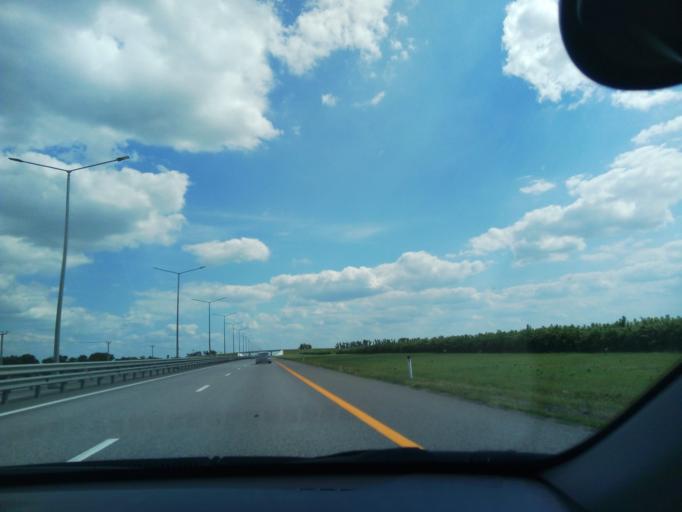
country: RU
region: Voronezj
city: Podkletnoye
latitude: 51.5760
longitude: 39.4672
